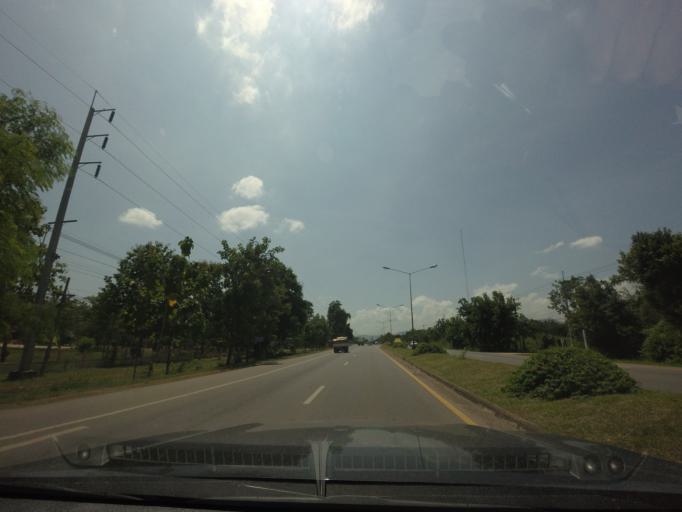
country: TH
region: Phetchabun
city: Lom Sak
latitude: 16.7004
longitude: 101.1725
